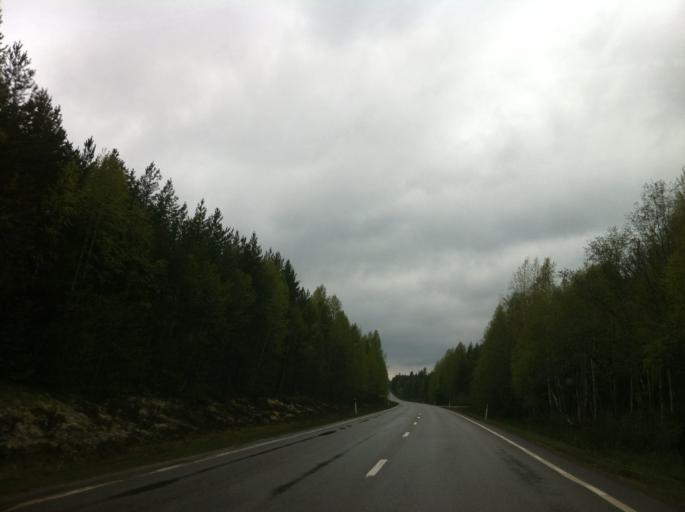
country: SE
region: Jaemtland
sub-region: Harjedalens Kommun
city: Sveg
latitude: 62.0972
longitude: 14.2300
